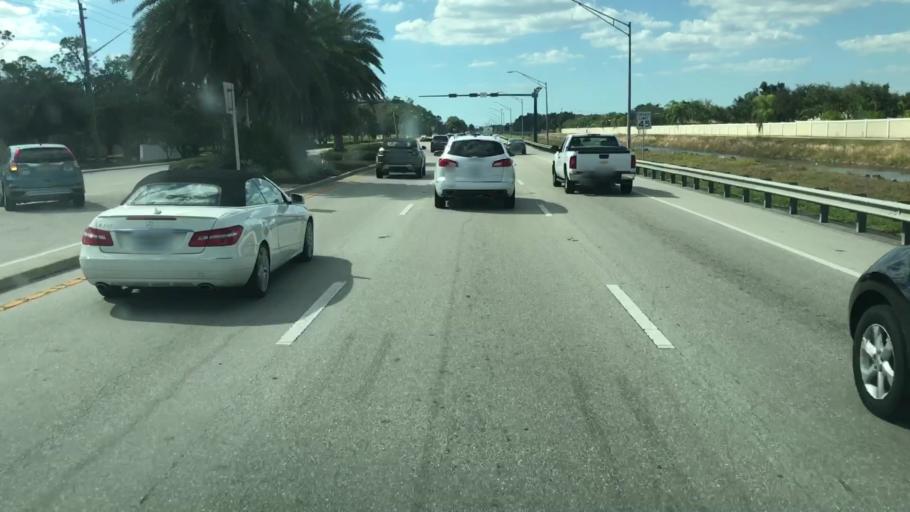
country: US
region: Florida
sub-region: Collier County
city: Vineyards
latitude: 26.2730
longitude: -81.7244
